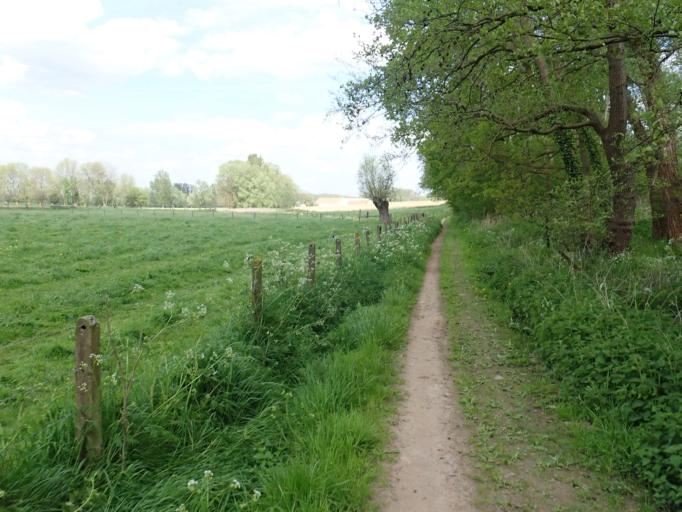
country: BE
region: Flanders
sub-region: Provincie Vlaams-Brabant
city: Asse
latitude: 50.9286
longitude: 4.1907
